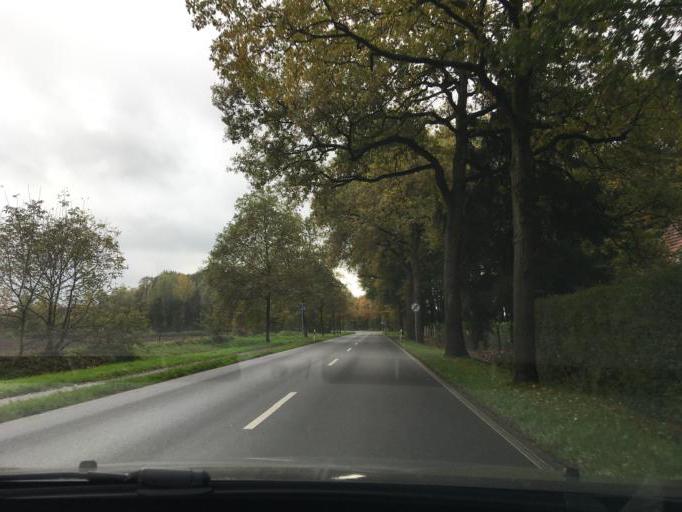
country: DE
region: North Rhine-Westphalia
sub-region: Regierungsbezirk Munster
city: Vreden
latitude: 52.0736
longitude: 6.7845
